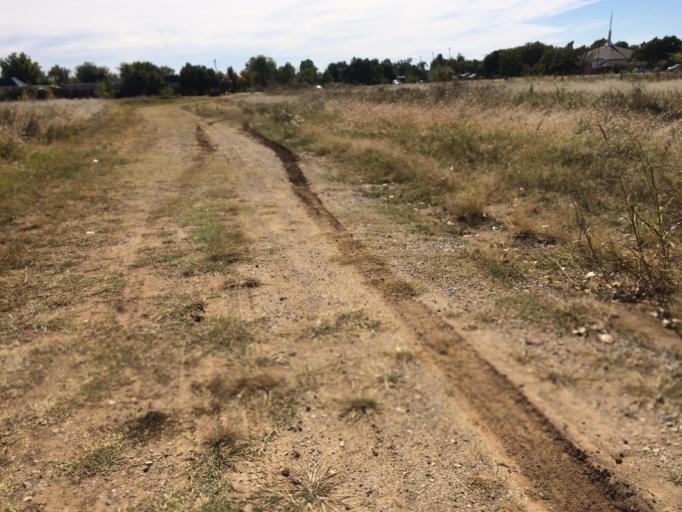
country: US
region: Oklahoma
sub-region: Cleveland County
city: Norman
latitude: 35.2213
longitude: -97.4283
